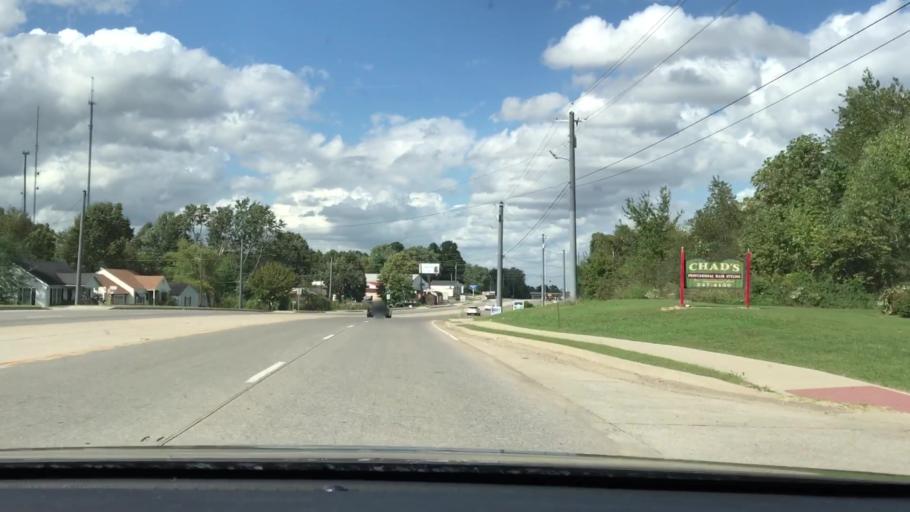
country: US
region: Kentucky
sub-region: Graves County
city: Mayfield
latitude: 36.7613
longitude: -88.6423
